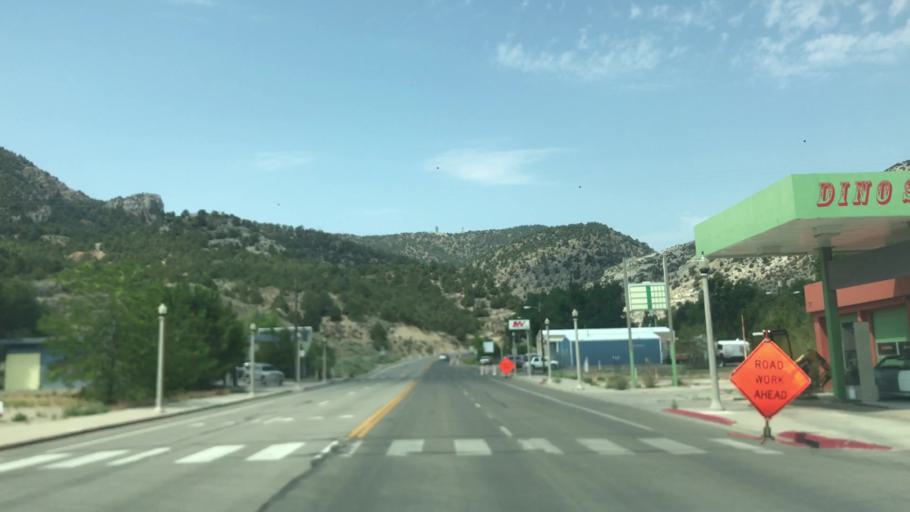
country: US
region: Nevada
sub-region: White Pine County
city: Ely
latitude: 39.2476
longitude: -114.8959
